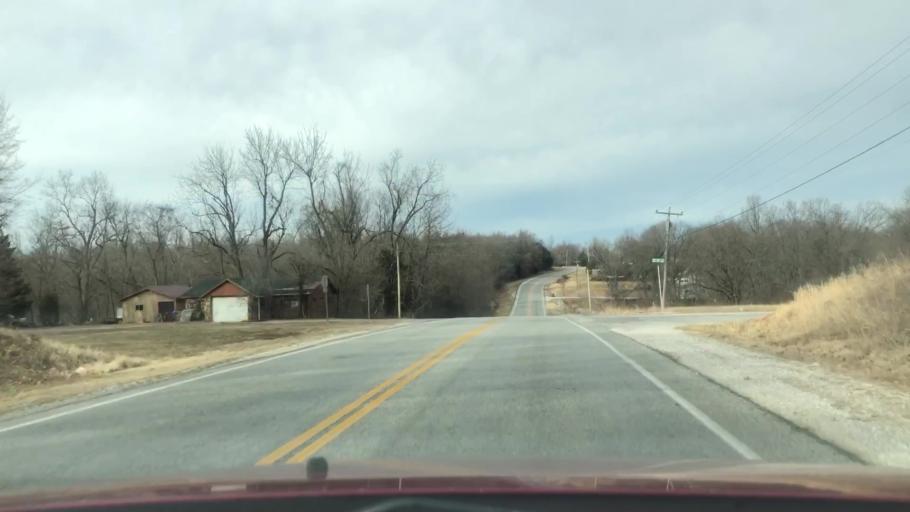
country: US
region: Missouri
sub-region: Greene County
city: Springfield
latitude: 37.2803
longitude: -93.2634
